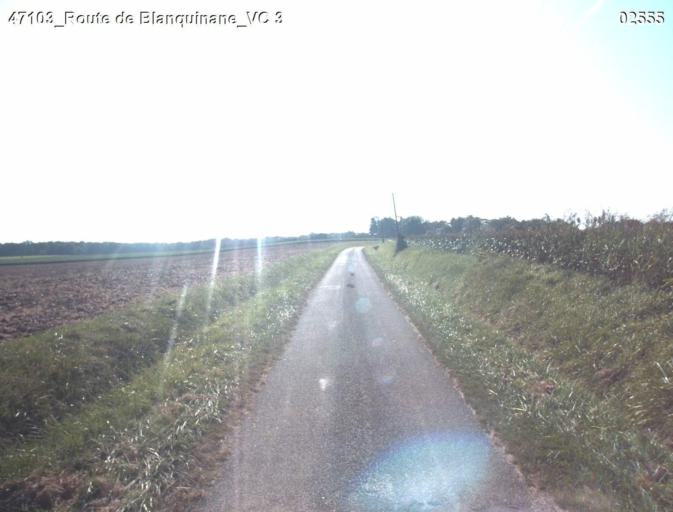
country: FR
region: Aquitaine
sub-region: Departement du Lot-et-Garonne
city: Nerac
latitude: 44.0884
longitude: 0.3357
